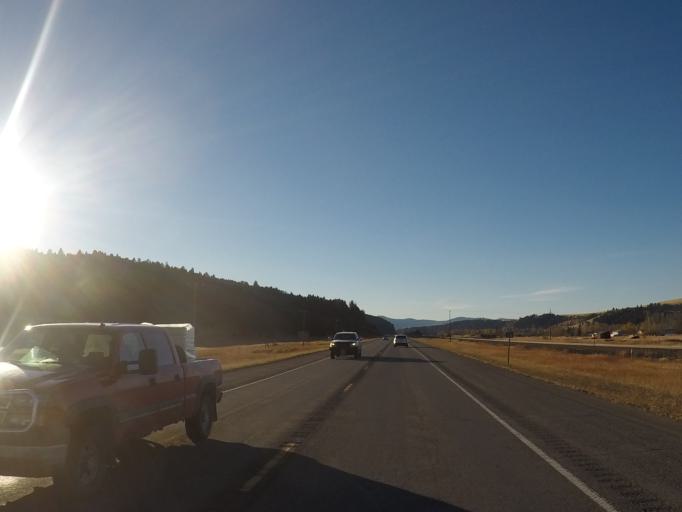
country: US
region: Montana
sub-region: Lewis and Clark County
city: Helena West Side
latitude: 46.5624
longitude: -112.4351
